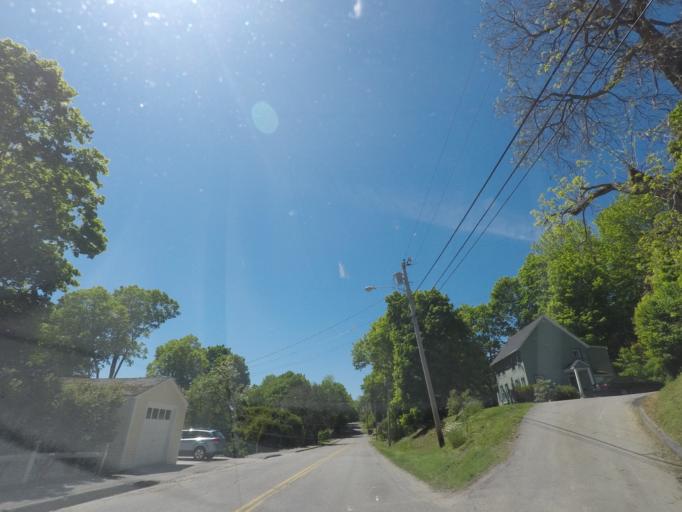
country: US
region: Maine
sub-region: Kennebec County
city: Hallowell
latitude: 44.2819
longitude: -69.7951
